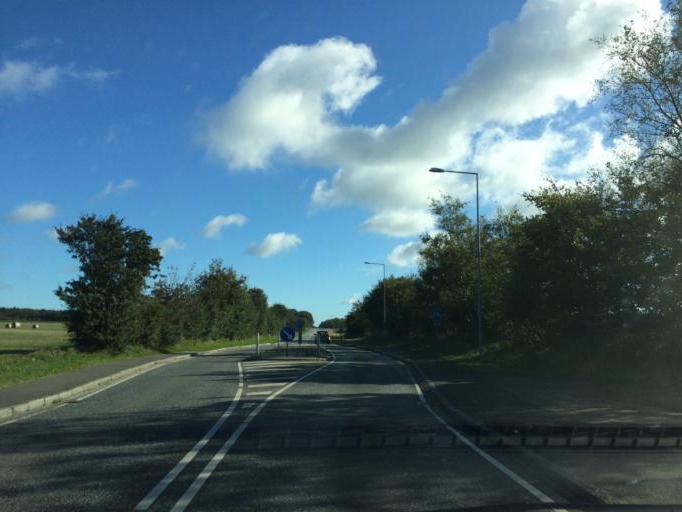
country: DK
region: Central Jutland
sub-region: Holstebro Kommune
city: Vinderup
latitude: 56.3914
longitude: 8.8143
